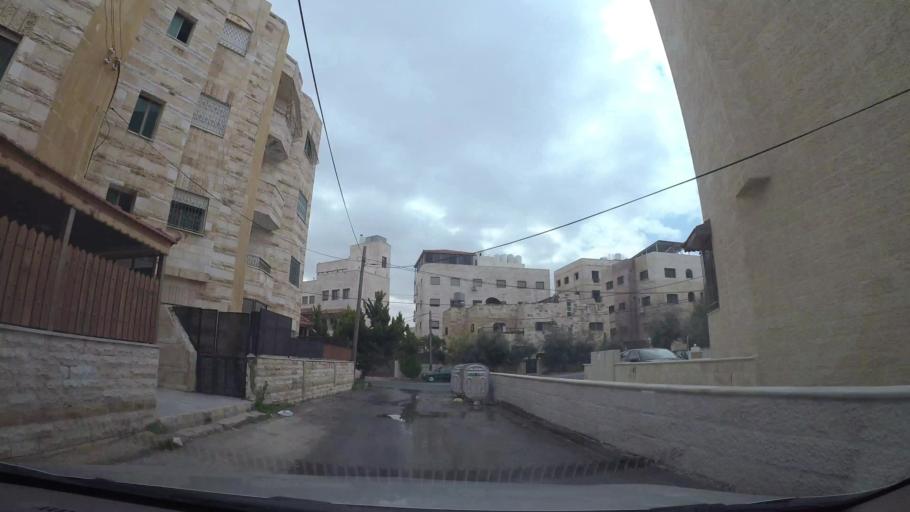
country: JO
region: Amman
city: Umm as Summaq
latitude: 31.8986
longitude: 35.8458
